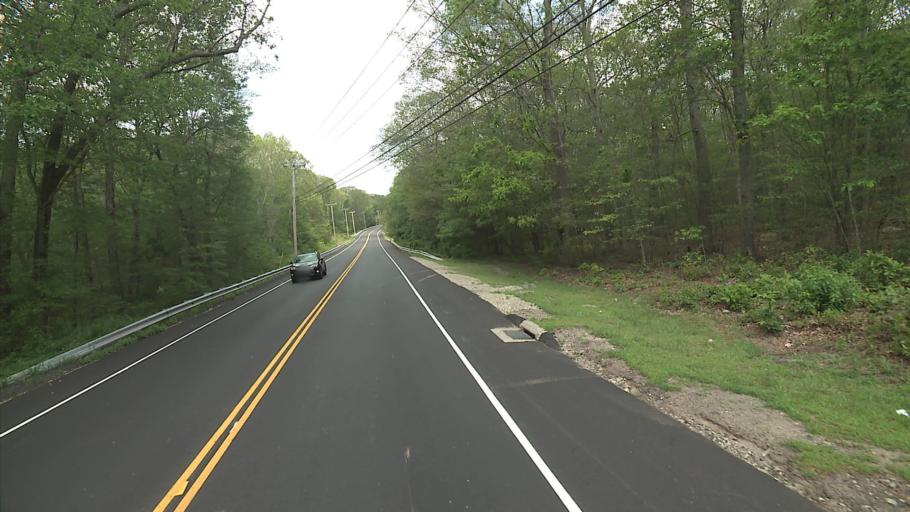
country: US
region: Connecticut
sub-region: New London County
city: Jewett City
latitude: 41.5784
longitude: -71.8901
